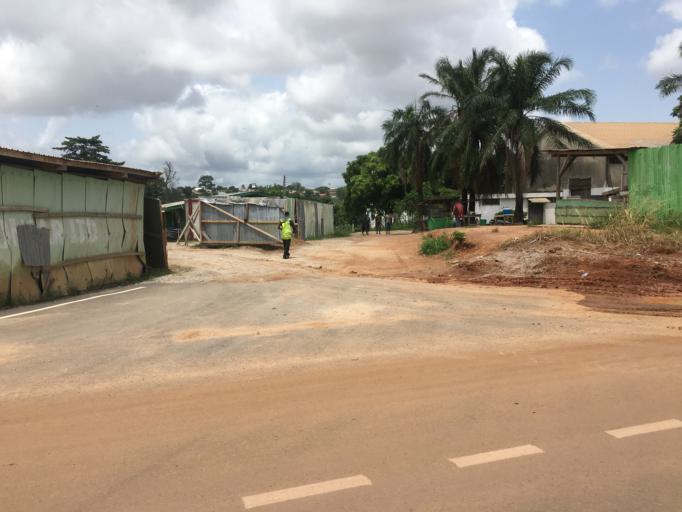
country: GH
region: Ashanti
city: Kumasi
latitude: 6.6691
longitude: -1.5753
